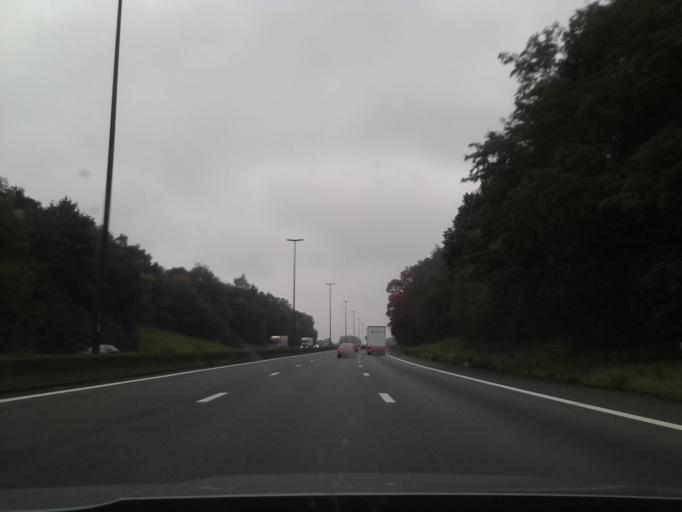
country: BE
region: Wallonia
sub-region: Province du Hainaut
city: Roeulx
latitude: 50.4807
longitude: 4.0493
